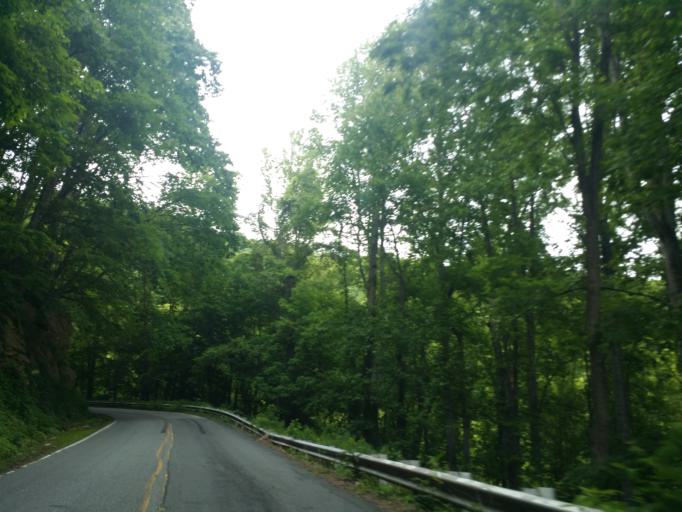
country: US
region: North Carolina
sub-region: Haywood County
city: West Canton
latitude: 35.7005
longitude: -82.8258
